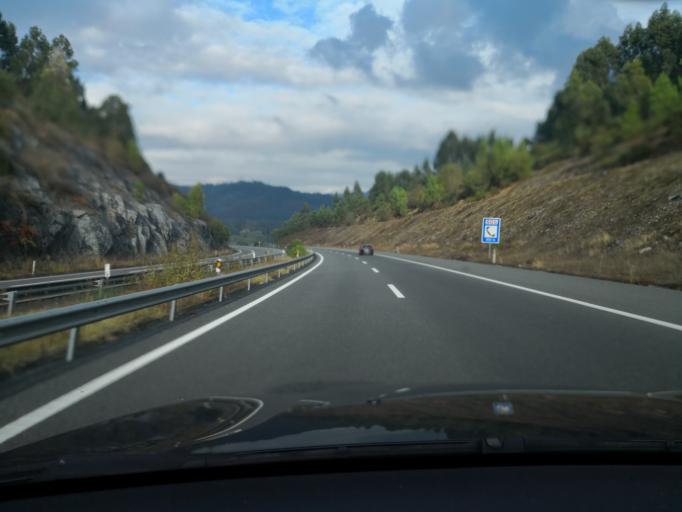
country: PT
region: Braga
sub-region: Guimaraes
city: Serzedo
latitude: 41.3981
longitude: -8.2357
